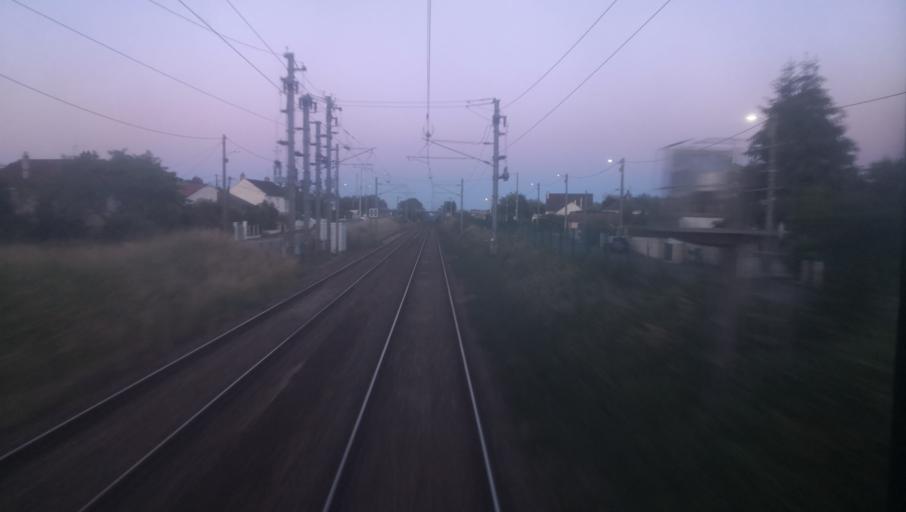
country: FR
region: Centre
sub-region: Departement du Loiret
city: Gien
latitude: 47.6894
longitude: 2.6454
